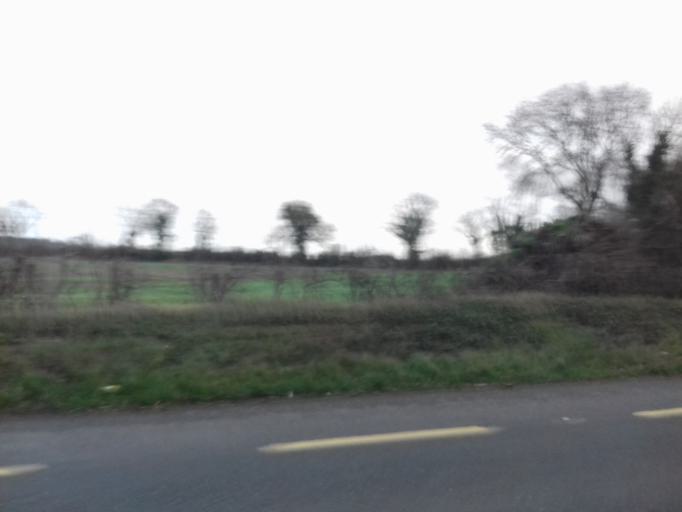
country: IE
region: Leinster
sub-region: An Mhi
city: Ratoath
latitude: 53.5483
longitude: -6.4328
